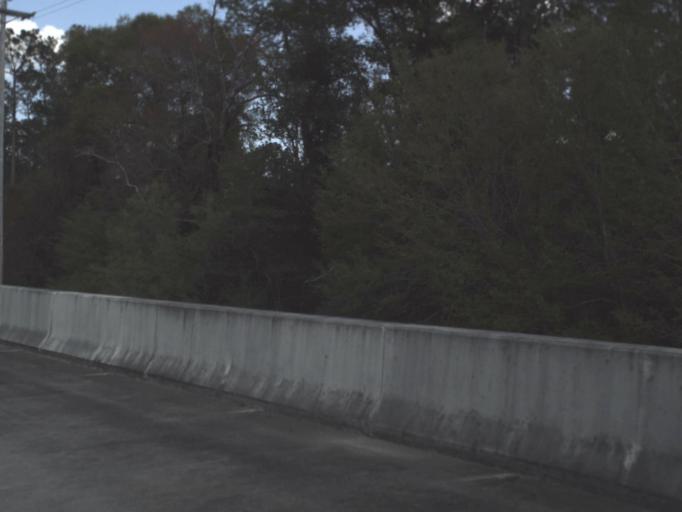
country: US
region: Florida
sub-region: Santa Rosa County
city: Point Baker
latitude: 30.8825
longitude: -86.9585
